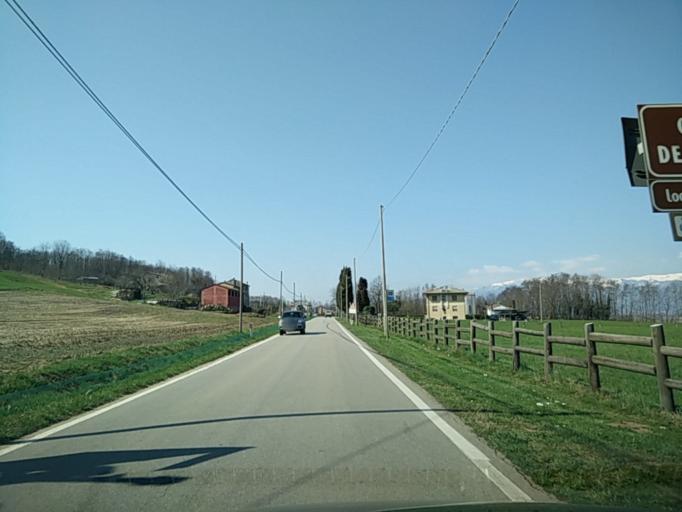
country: IT
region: Veneto
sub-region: Provincia di Treviso
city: Moriago della Battaglia
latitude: 45.8331
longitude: 12.1092
